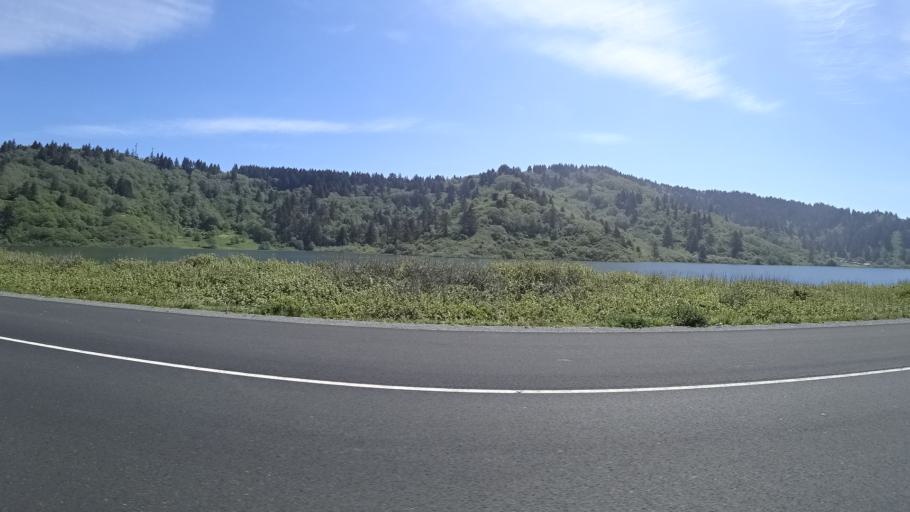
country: US
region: California
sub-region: Humboldt County
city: Westhaven-Moonstone
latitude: 41.2732
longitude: -124.0951
